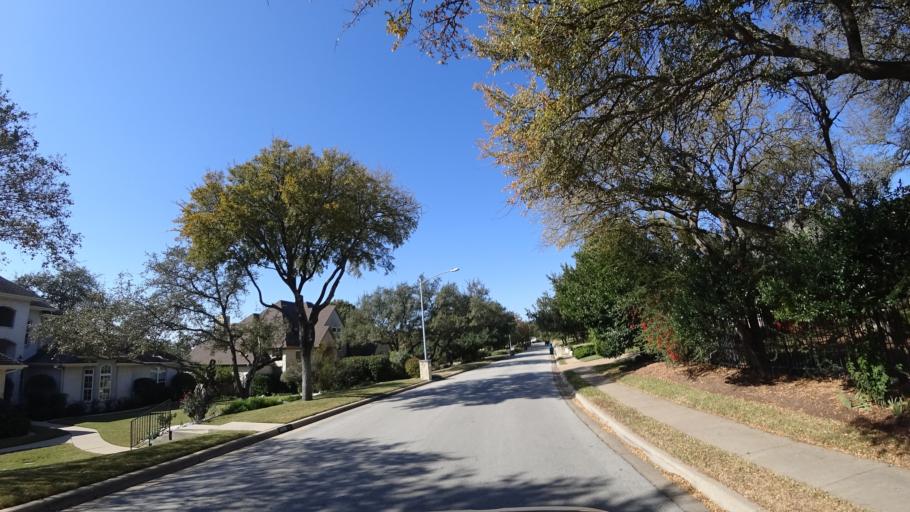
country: US
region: Texas
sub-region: Travis County
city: Lost Creek
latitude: 30.3737
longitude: -97.8494
